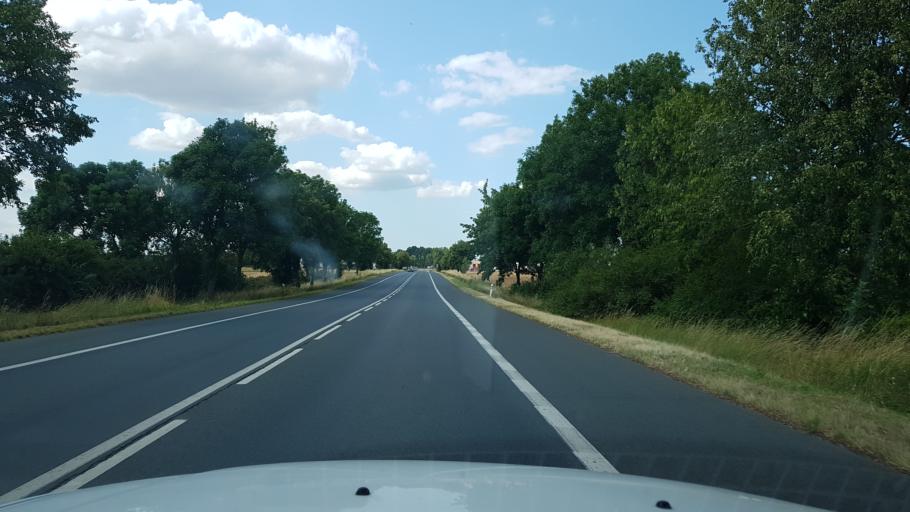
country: PL
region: West Pomeranian Voivodeship
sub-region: Powiat pyrzycki
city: Pyrzyce
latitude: 53.1211
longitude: 14.8911
